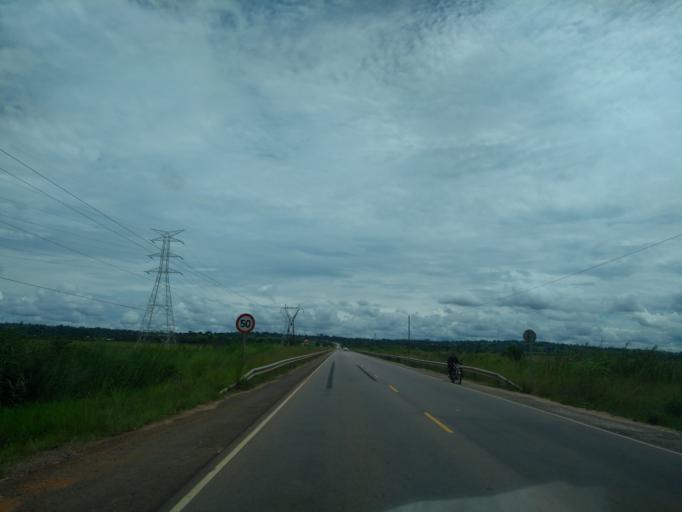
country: UG
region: Central Region
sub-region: Gomba District
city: Kanoni
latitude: -0.0313
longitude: 32.0115
